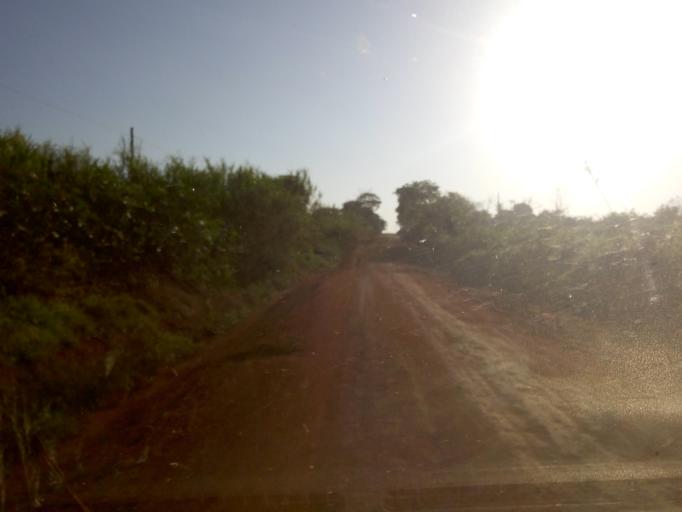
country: UG
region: Western Region
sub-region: Masindi District
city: Masindi
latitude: 1.7783
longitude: 31.8492
